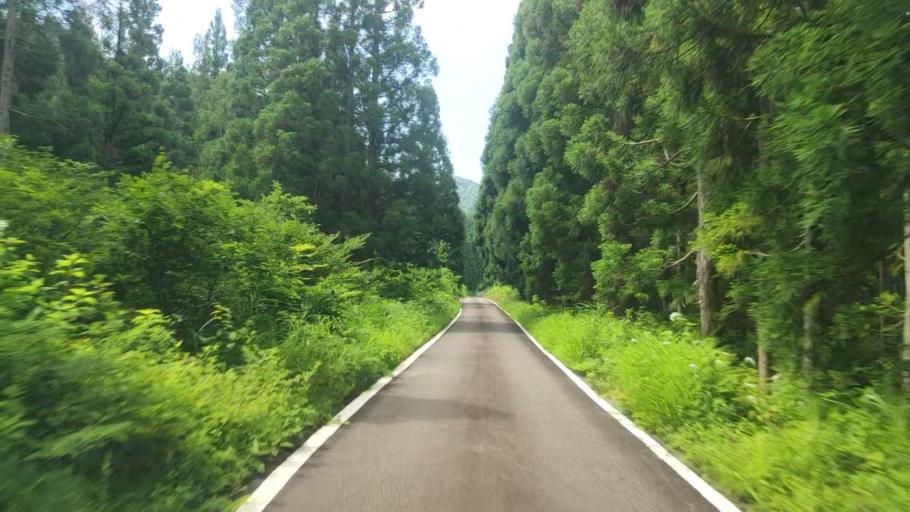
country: JP
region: Fukui
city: Katsuyama
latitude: 36.1683
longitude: 136.5237
